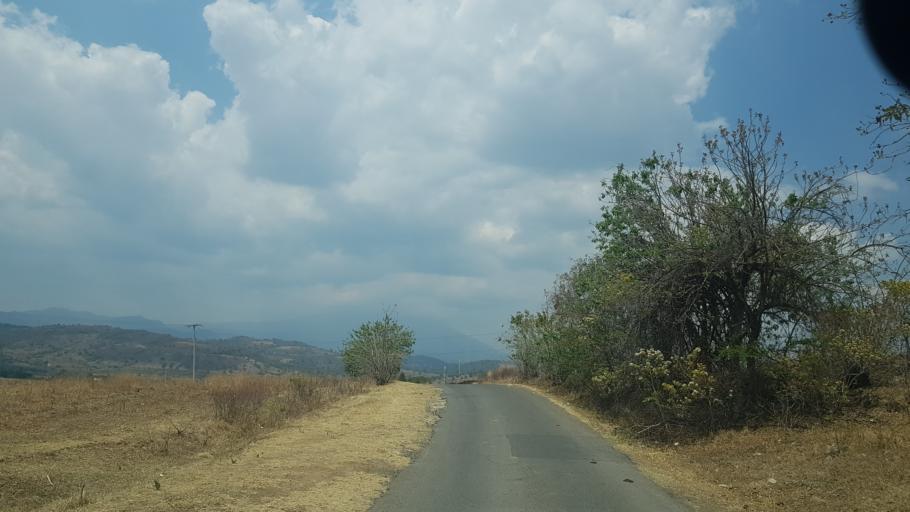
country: MX
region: Puebla
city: San Juan Amecac
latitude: 18.8176
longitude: -98.6238
